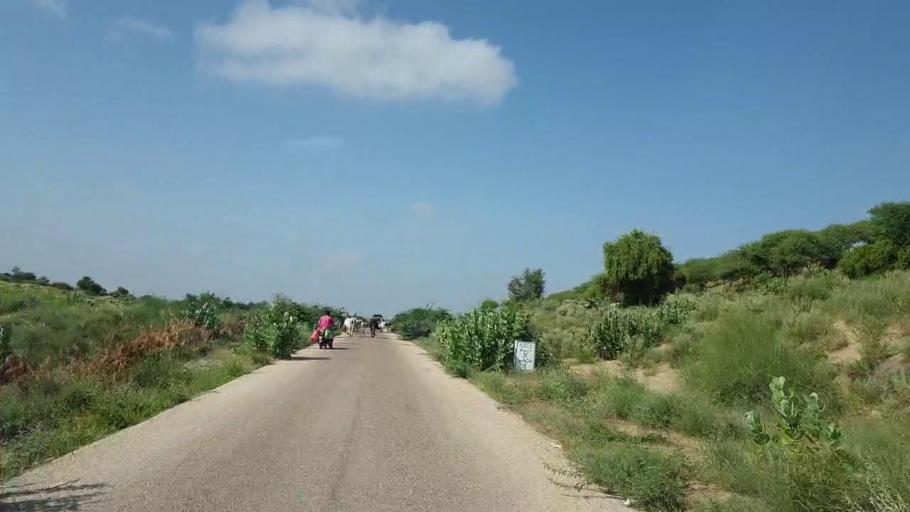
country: PK
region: Sindh
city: Mithi
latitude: 24.5393
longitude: 69.8644
